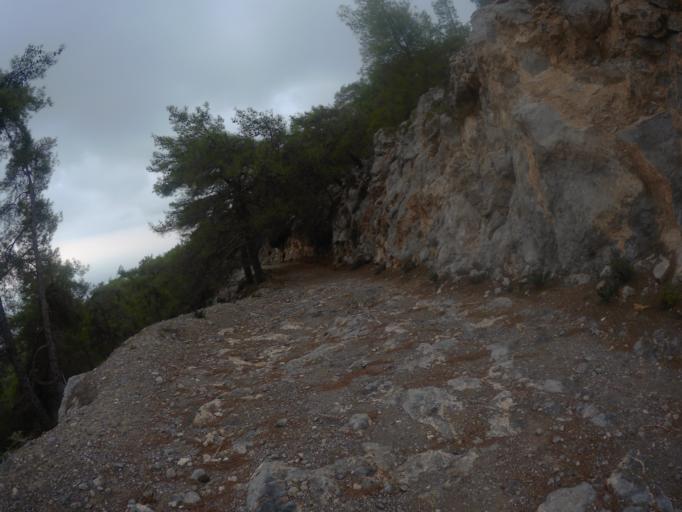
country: CY
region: Ammochostos
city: Lefkonoiko
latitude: 35.2962
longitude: 33.5630
